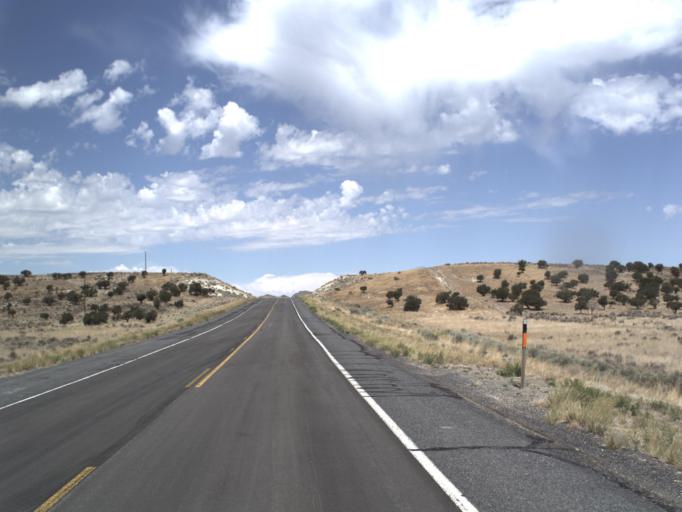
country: US
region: Utah
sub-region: Utah County
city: Eagle Mountain
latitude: 40.0643
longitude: -112.3196
